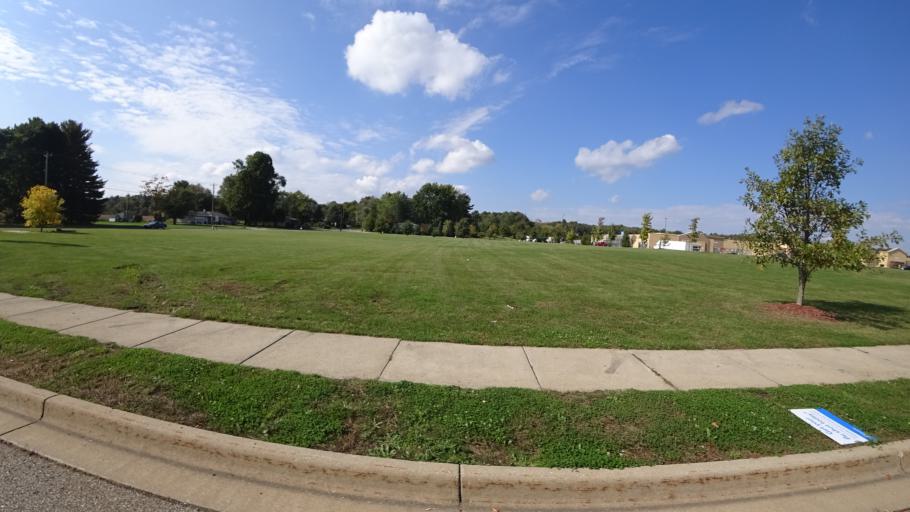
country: US
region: Michigan
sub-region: Saint Joseph County
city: Three Rivers
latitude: 41.9402
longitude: -85.6541
